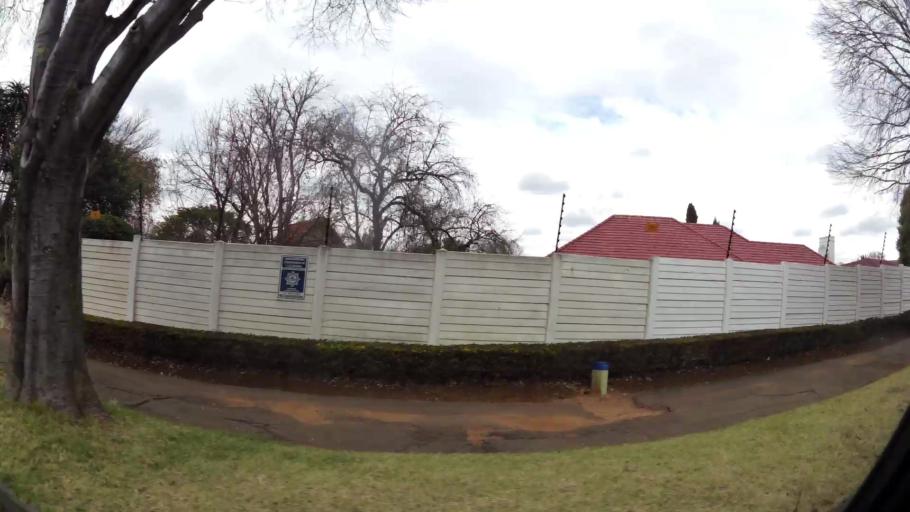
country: ZA
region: Gauteng
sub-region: City of Johannesburg Metropolitan Municipality
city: Johannesburg
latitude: -26.1479
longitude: 27.9925
